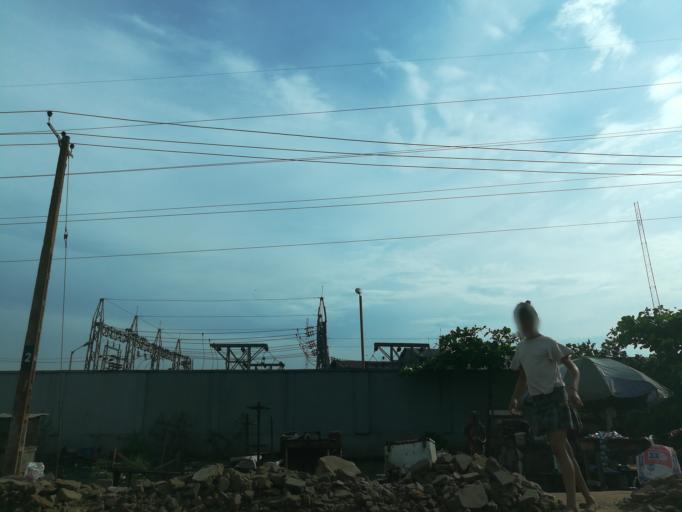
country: NG
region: Lagos
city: Ojota
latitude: 6.6095
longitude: 3.4222
